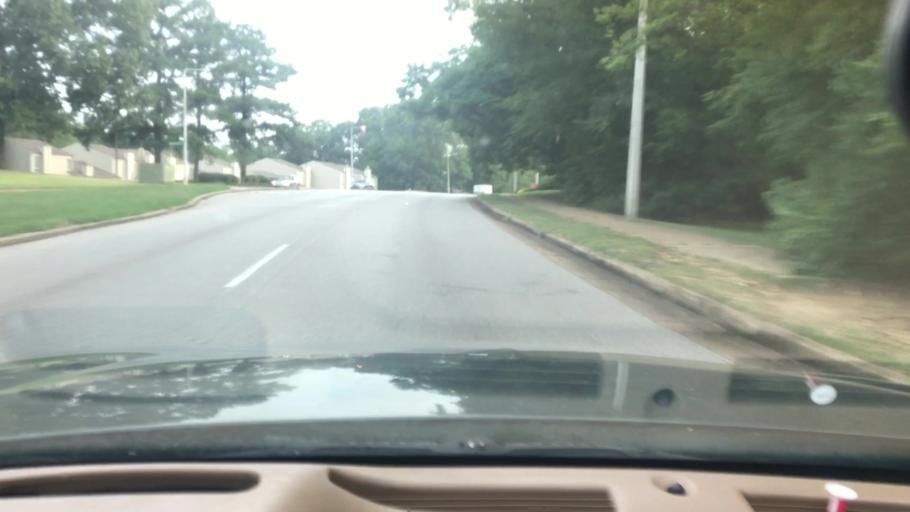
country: US
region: Tennessee
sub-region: Shelby County
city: Bartlett
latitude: 35.1761
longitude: -89.8712
